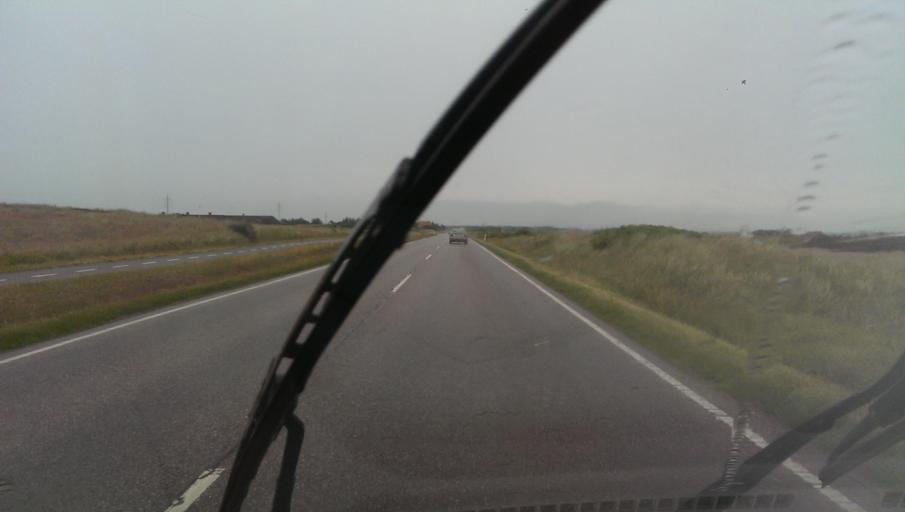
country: DK
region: Central Jutland
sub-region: Ringkobing-Skjern Kommune
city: Hvide Sande
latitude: 56.0719
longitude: 8.1212
